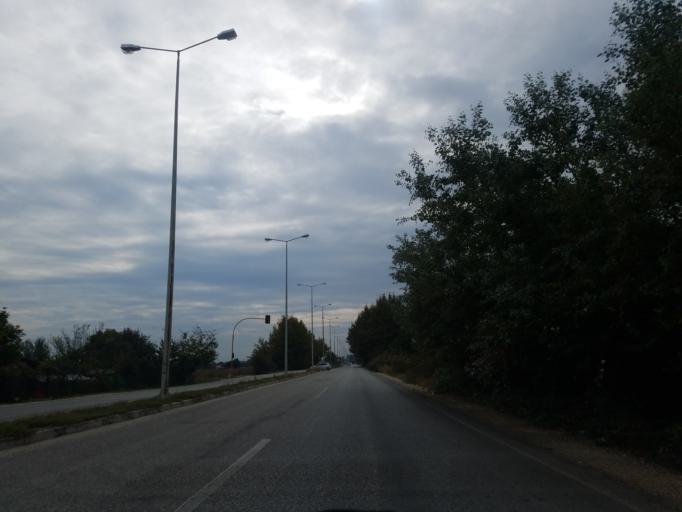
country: GR
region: Thessaly
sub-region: Trikala
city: Pyrgetos
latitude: 39.5286
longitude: 21.7455
